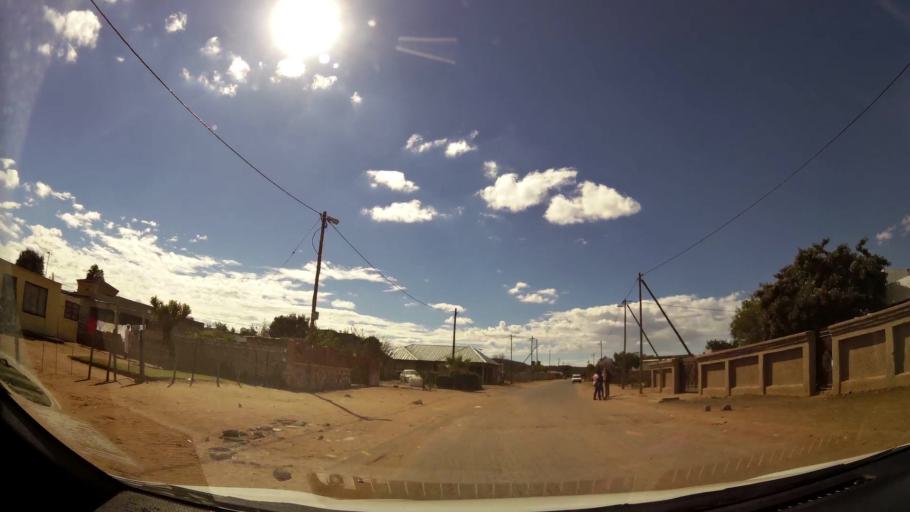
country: ZA
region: Limpopo
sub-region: Waterberg District Municipality
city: Bela-Bela
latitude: -24.8778
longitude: 28.3230
